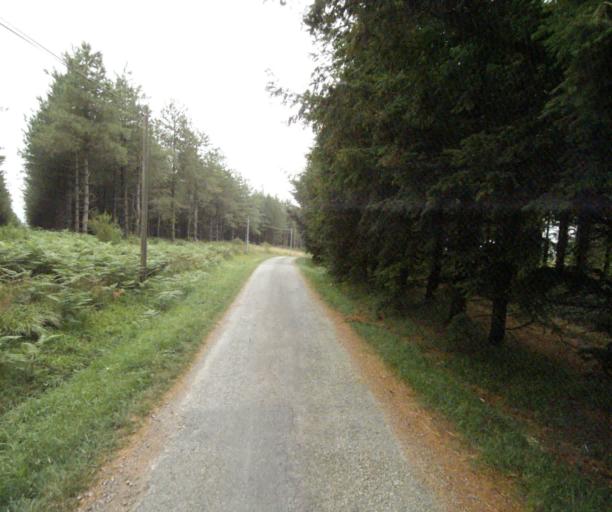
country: FR
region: Midi-Pyrenees
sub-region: Departement du Tarn
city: Soreze
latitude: 43.4175
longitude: 2.0477
